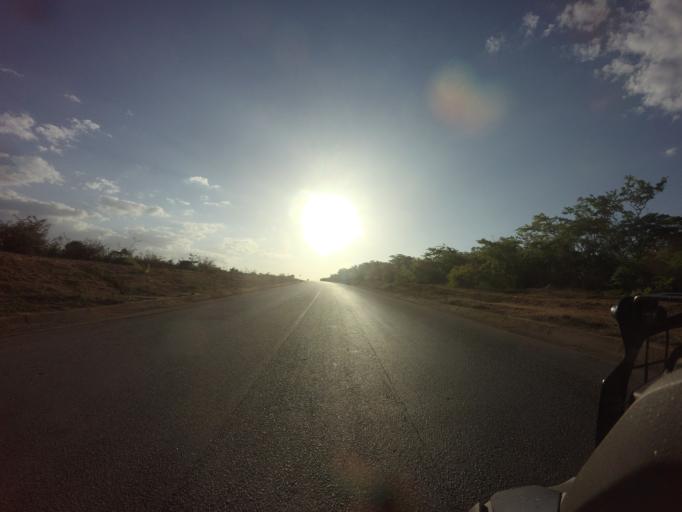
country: AO
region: Huila
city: Lubango
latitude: -14.7872
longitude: 13.7132
